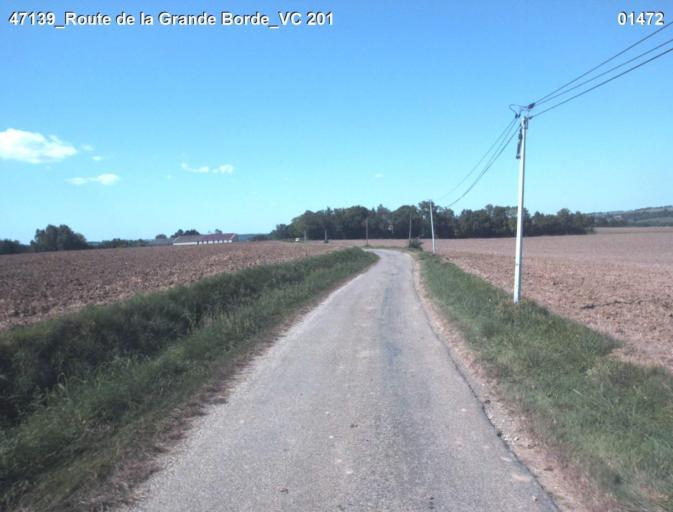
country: FR
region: Aquitaine
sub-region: Departement du Lot-et-Garonne
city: Nerac
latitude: 44.0730
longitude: 0.3857
